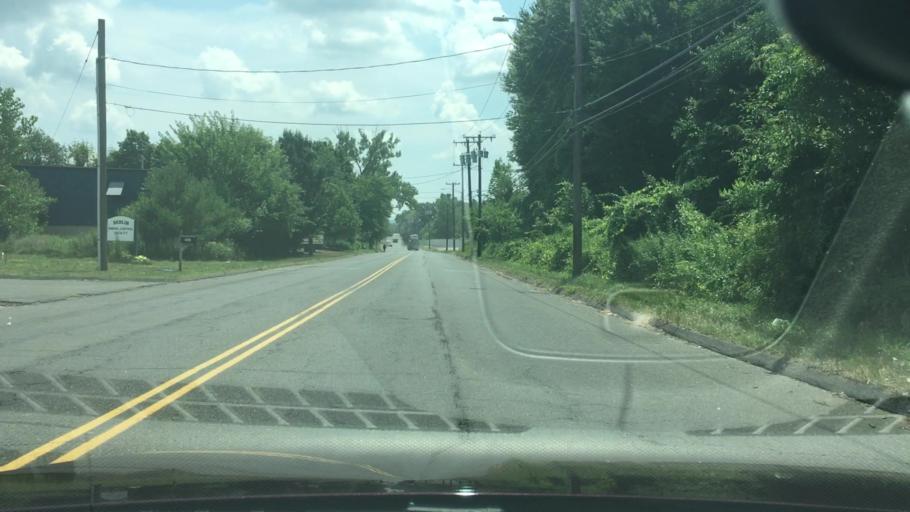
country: US
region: Connecticut
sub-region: Hartford County
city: Kensington
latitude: 41.6470
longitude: -72.7513
